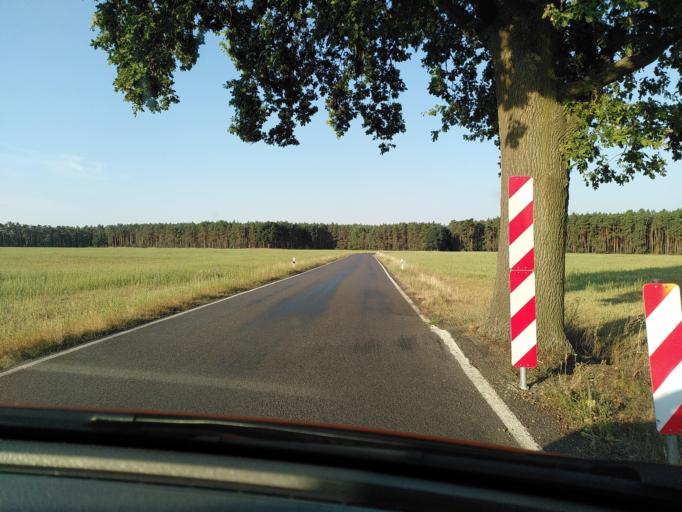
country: DE
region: Saxony
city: Horka
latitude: 51.2995
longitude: 14.2801
